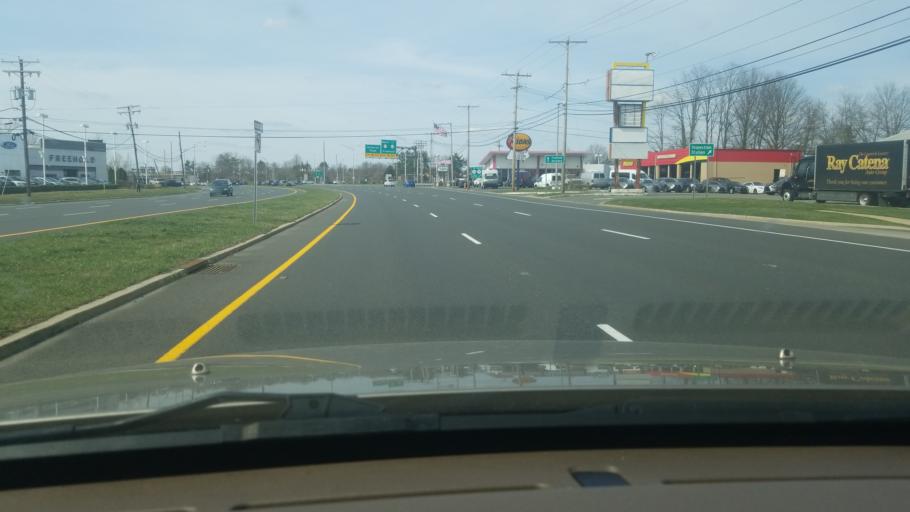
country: US
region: New Jersey
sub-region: Monmouth County
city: Freehold
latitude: 40.2377
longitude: -74.2743
